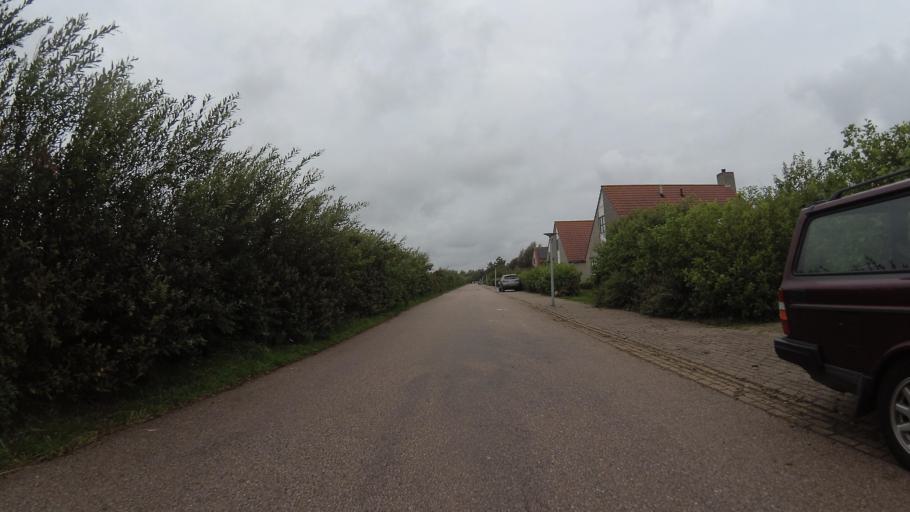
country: NL
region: North Holland
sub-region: Gemeente Den Helder
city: Den Helder
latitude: 52.8858
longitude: 4.7269
